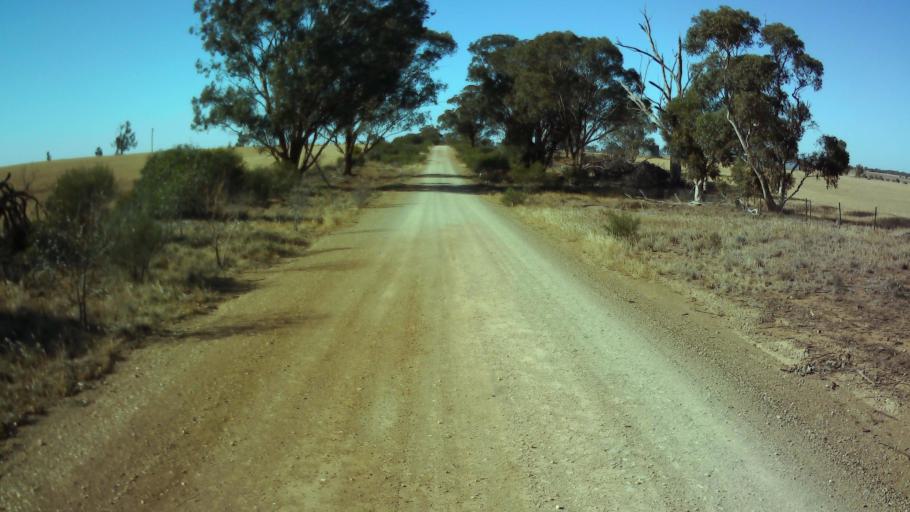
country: AU
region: New South Wales
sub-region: Weddin
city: Grenfell
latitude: -33.8806
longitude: 147.8824
